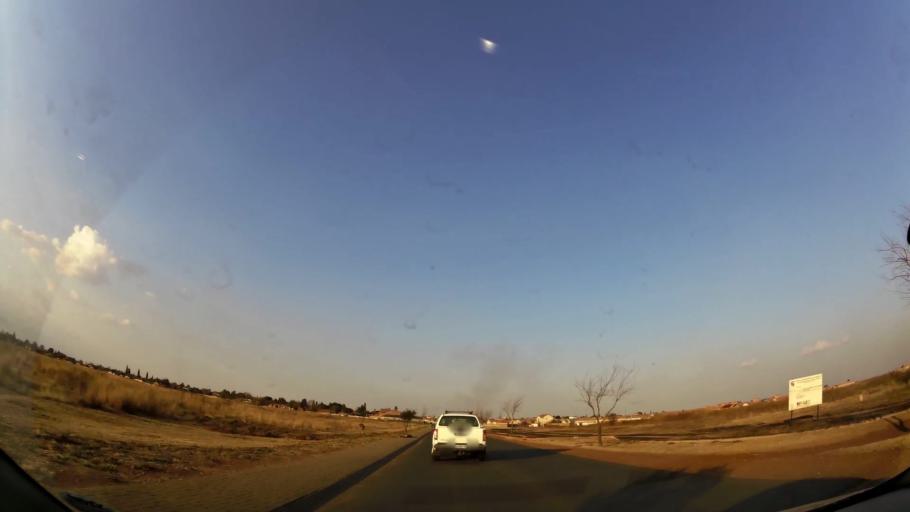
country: ZA
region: Gauteng
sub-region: Ekurhuleni Metropolitan Municipality
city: Germiston
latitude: -26.3081
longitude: 28.2338
